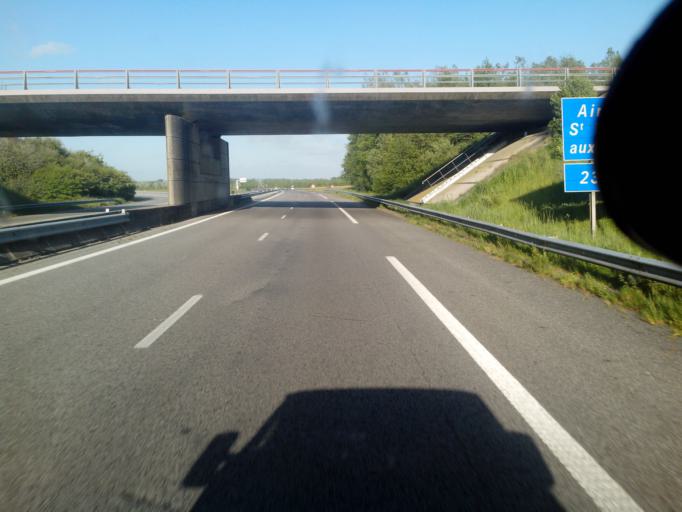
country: FR
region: Haute-Normandie
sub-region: Departement de la Seine-Maritime
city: Yerville
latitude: 49.6521
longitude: 0.8445
